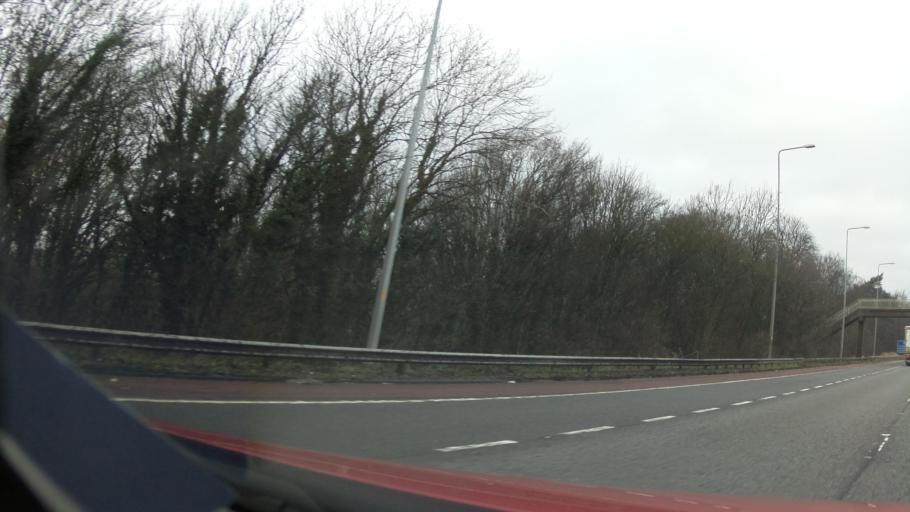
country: GB
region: England
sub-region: Lancashire
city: Coppull
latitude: 53.6335
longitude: -2.6915
